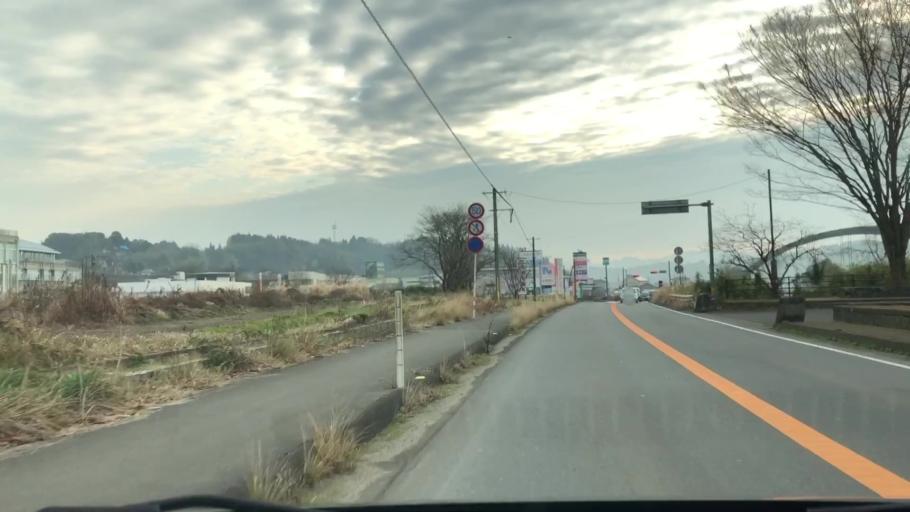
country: JP
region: Oita
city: Takedamachi
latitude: 32.9695
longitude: 131.4722
